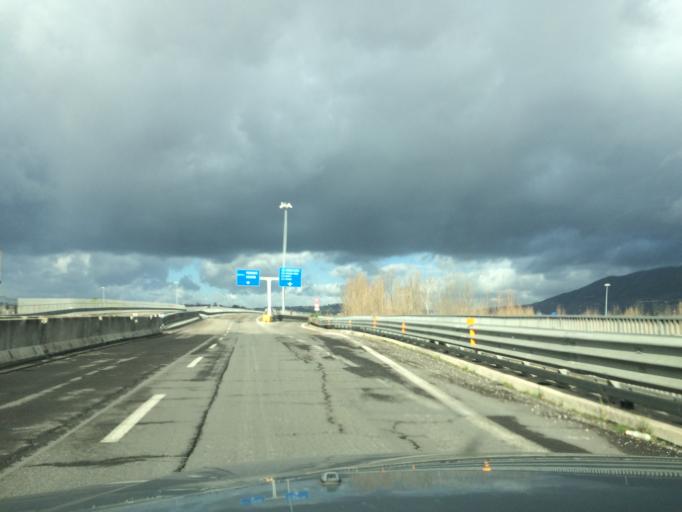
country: IT
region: Umbria
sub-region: Provincia di Terni
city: Terni
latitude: 42.5658
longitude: 12.5787
